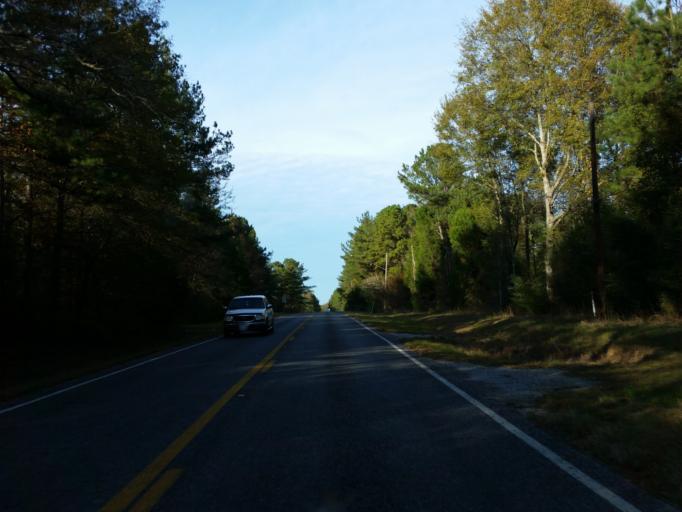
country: US
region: Mississippi
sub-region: Clarke County
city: Stonewall
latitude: 32.0450
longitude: -88.8831
